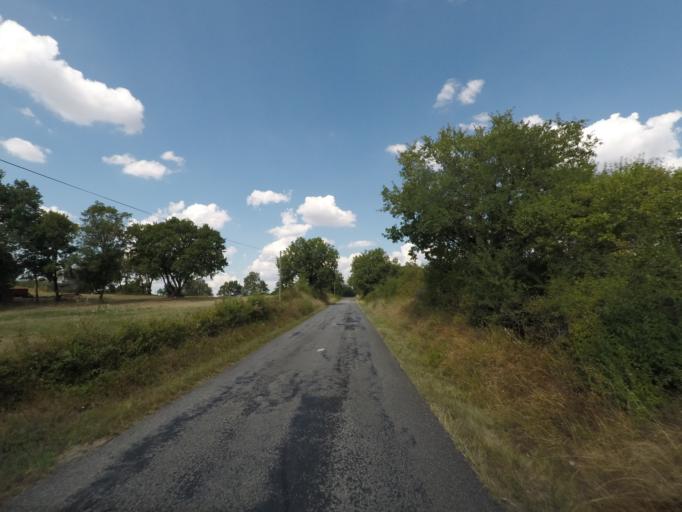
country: FR
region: Midi-Pyrenees
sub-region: Departement du Lot
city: Le Vigan
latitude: 44.6097
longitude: 1.5887
